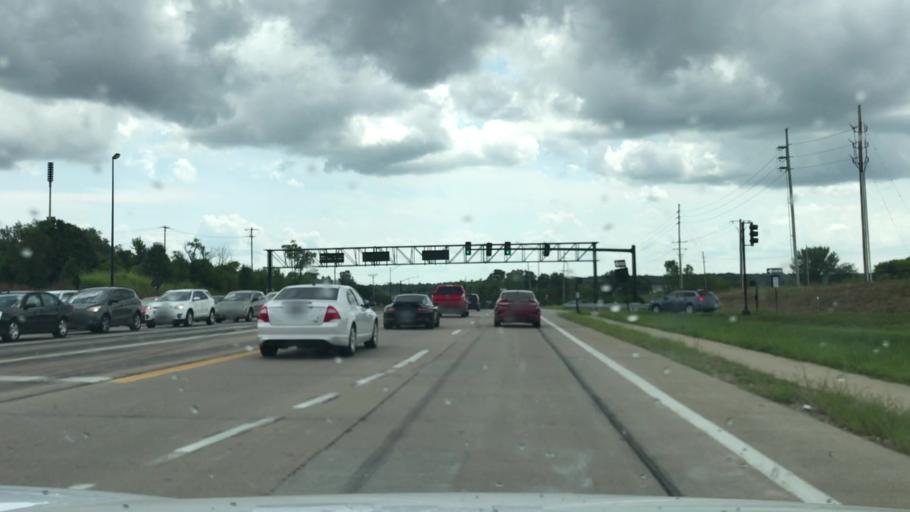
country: US
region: Missouri
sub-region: Saint Charles County
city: Dardenne Prairie
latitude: 38.7530
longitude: -90.7004
